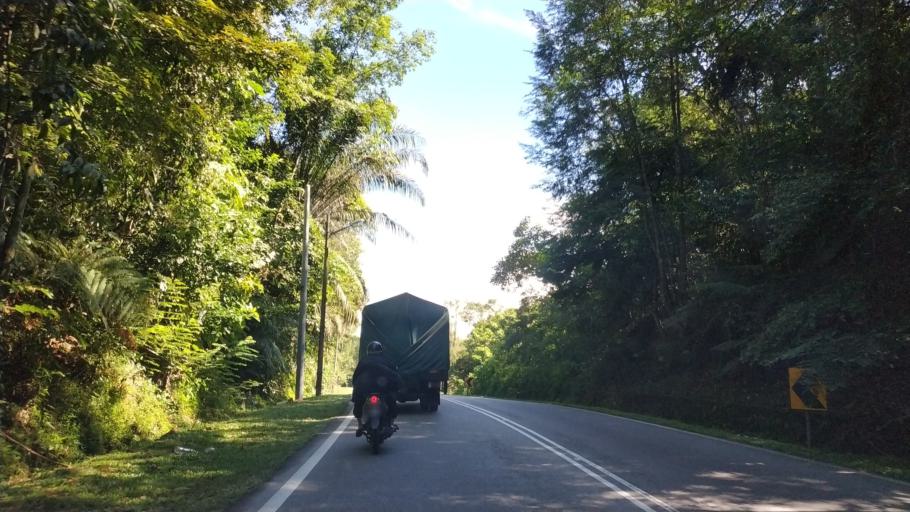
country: MY
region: Kedah
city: Kulim
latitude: 5.3287
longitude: 100.5330
